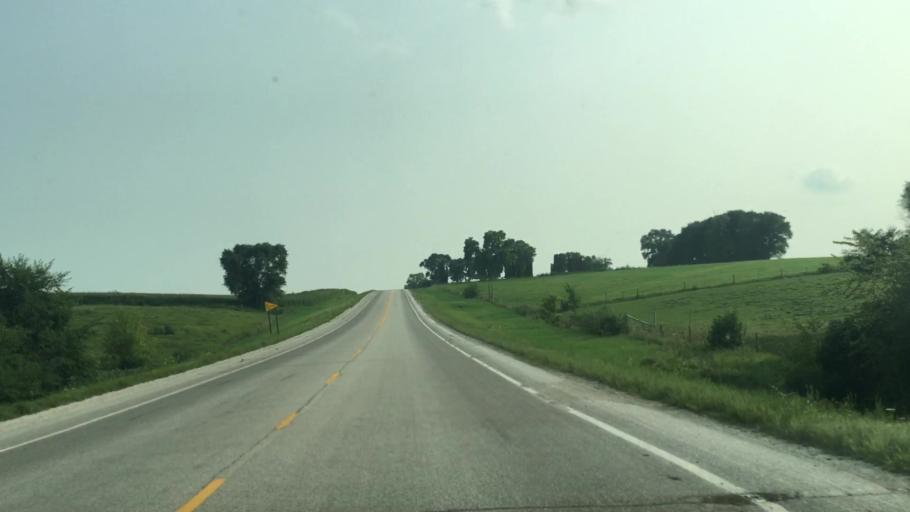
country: US
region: Minnesota
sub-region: Fillmore County
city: Harmony
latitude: 43.5431
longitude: -91.9296
